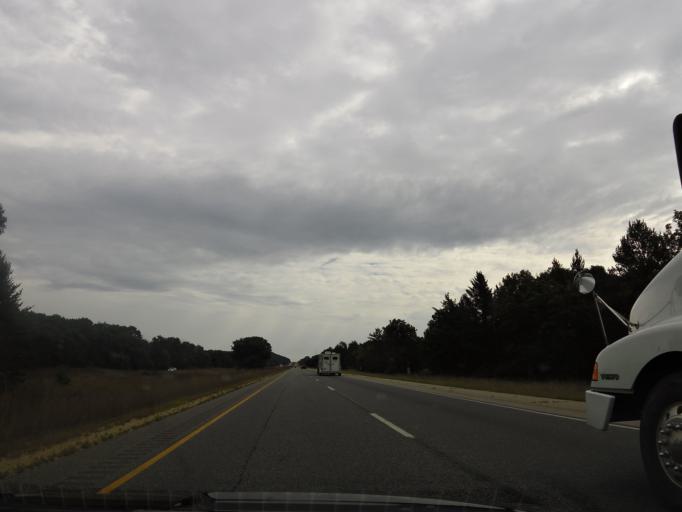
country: US
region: Wisconsin
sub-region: Monroe County
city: Tomah
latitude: 43.9398
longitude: -90.6525
